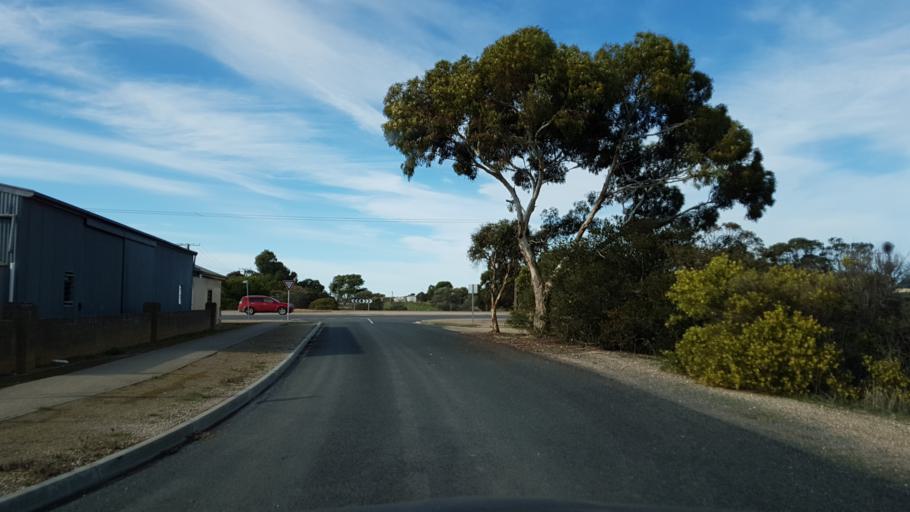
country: AU
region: South Australia
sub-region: Murray Bridge
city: Tailem Bend
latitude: -35.2518
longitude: 139.4539
